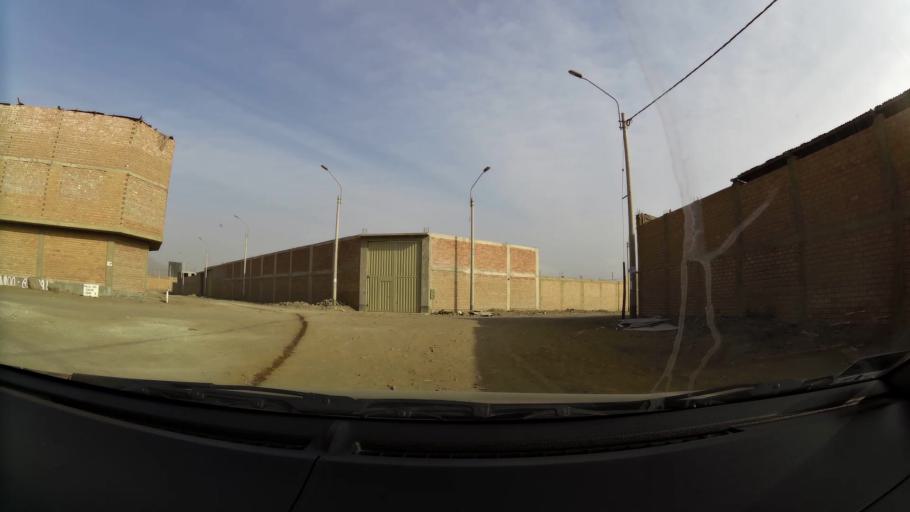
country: PE
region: Lima
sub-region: Lima
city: Santa Rosa
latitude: -11.7537
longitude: -77.1587
